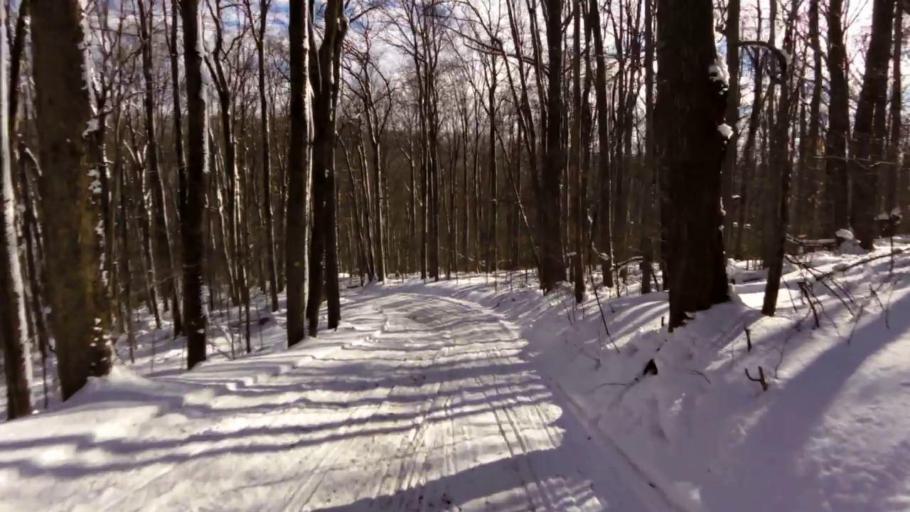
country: US
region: New York
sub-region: Cattaraugus County
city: Salamanca
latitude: 42.0687
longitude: -78.6741
